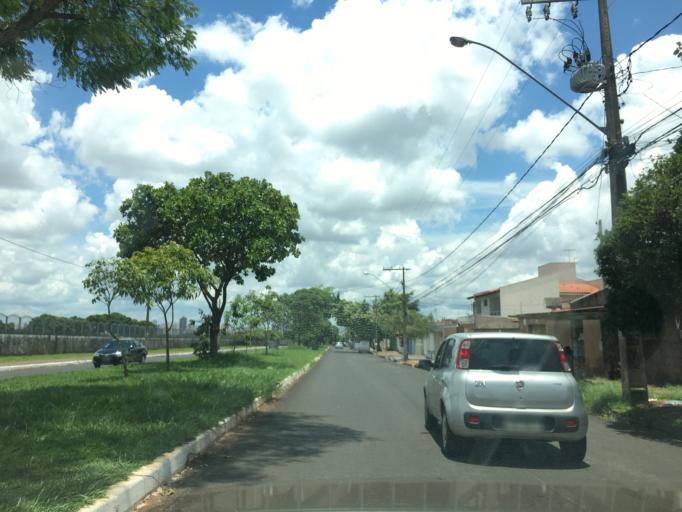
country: BR
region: Minas Gerais
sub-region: Uberlandia
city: Uberlandia
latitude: -18.9362
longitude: -48.3108
